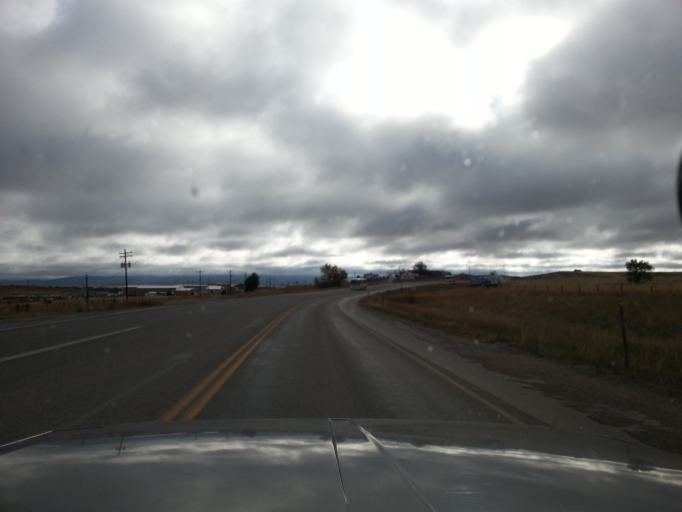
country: US
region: Wyoming
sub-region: Converse County
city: Douglas
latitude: 42.7833
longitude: -105.3719
